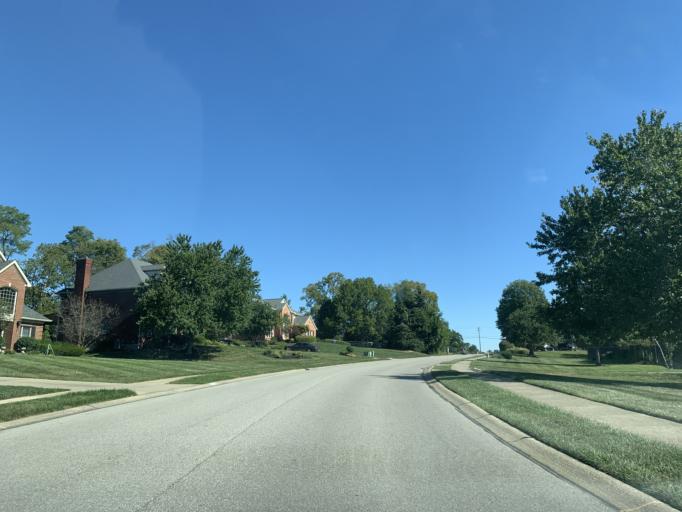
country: US
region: Kentucky
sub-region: Boone County
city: Francisville
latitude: 39.1027
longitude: -84.7253
